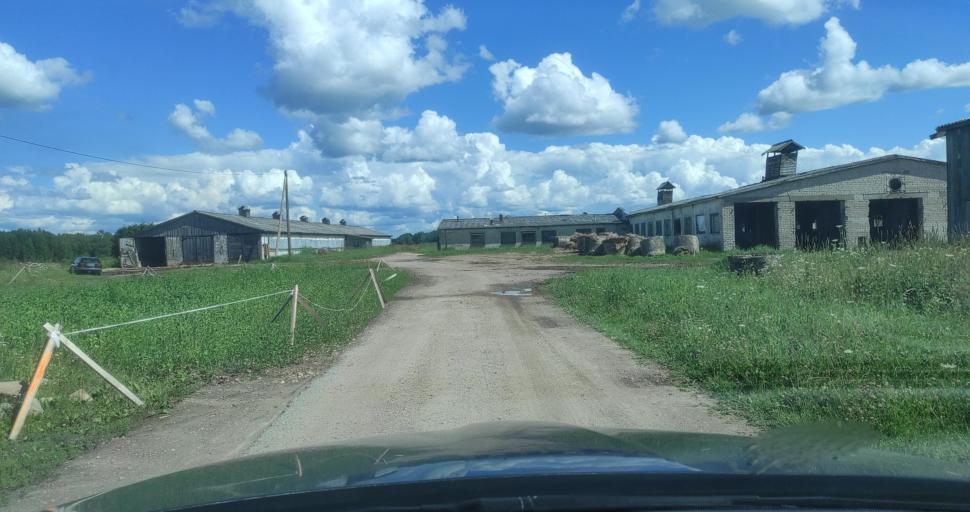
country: LV
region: Kuldigas Rajons
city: Kuldiga
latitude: 57.0025
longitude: 22.1290
